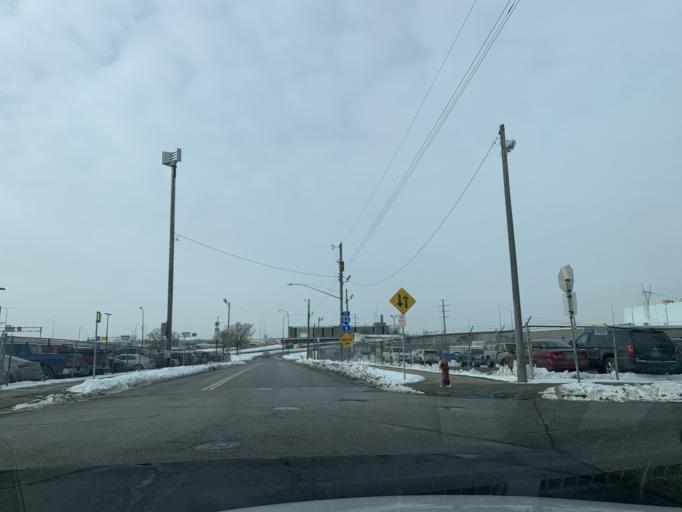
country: US
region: Minnesota
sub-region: Hennepin County
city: Minneapolis
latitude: 44.9760
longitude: -93.2840
